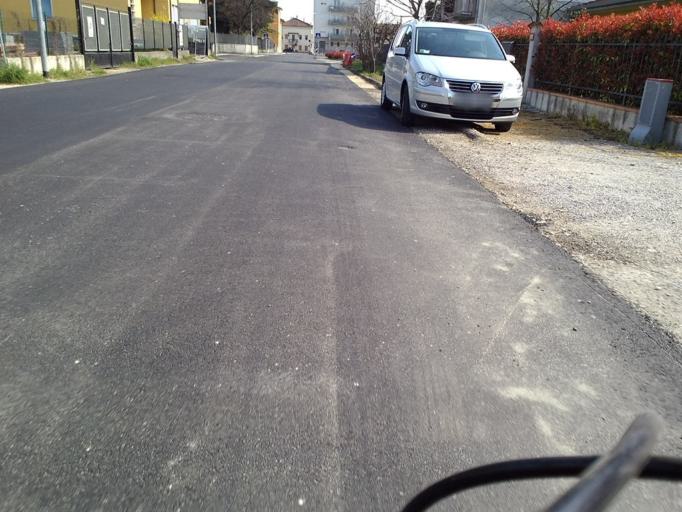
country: IT
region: Veneto
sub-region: Provincia di Verona
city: Dossobuono
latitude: 45.4072
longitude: 10.9277
